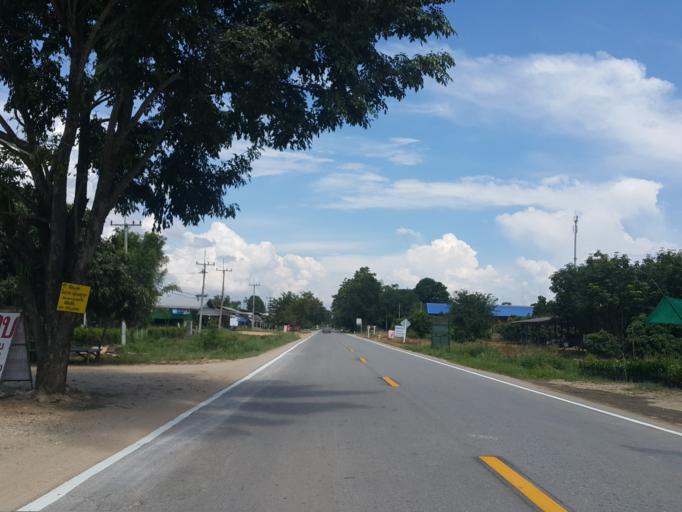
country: TH
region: Chiang Mai
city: Phrao
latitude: 19.2433
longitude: 99.1854
